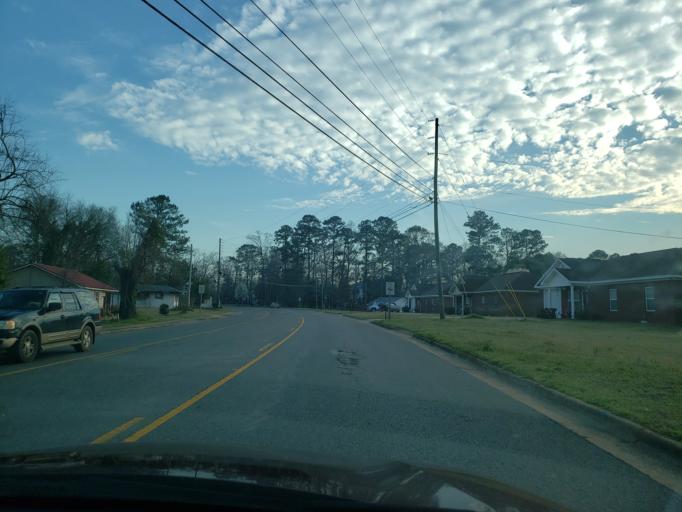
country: US
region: Alabama
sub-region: Hale County
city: Greensboro
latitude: 32.7153
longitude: -87.5956
